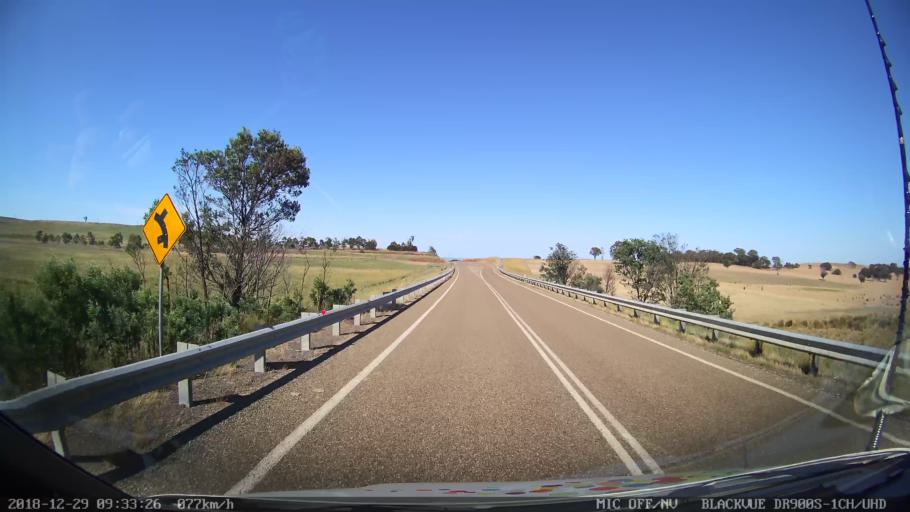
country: AU
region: New South Wales
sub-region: Upper Lachlan Shire
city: Crookwell
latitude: -34.6256
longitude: 149.3468
